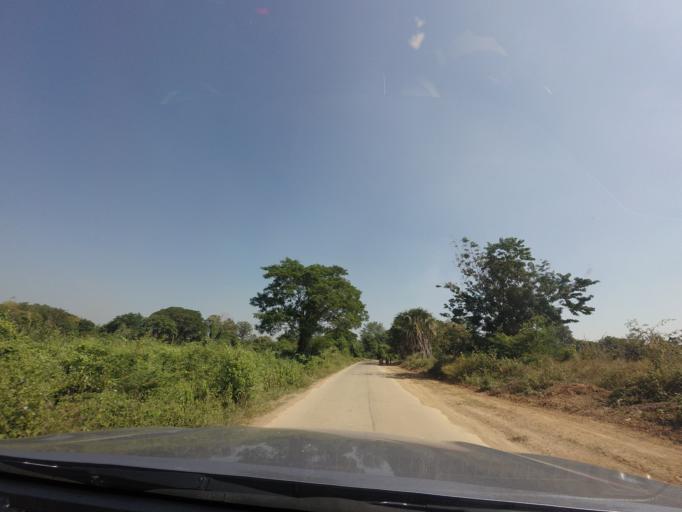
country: TH
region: Sukhothai
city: Sawankhalok
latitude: 17.2767
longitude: 99.8220
